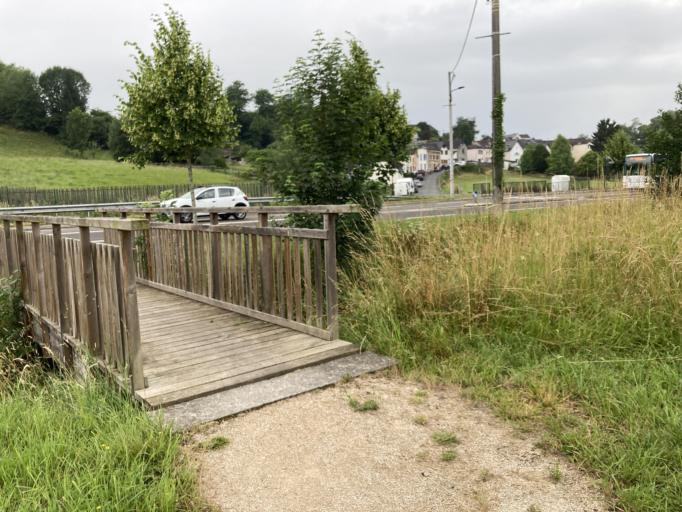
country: FR
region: Aquitaine
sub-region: Departement des Pyrenees-Atlantiques
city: Oloron-Sainte-Marie
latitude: 43.1940
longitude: -0.5989
